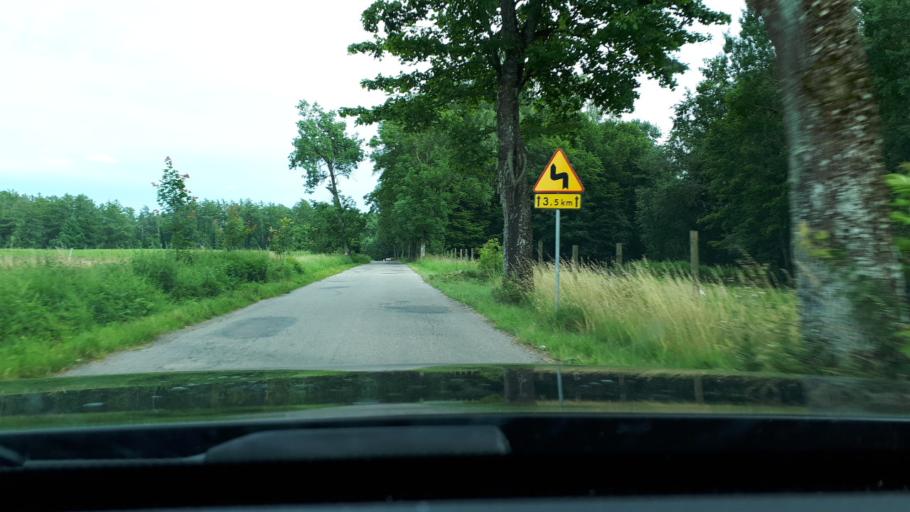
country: PL
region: Warmian-Masurian Voivodeship
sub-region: Powiat ostrodzki
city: Gierzwald
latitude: 53.6394
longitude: 20.1156
